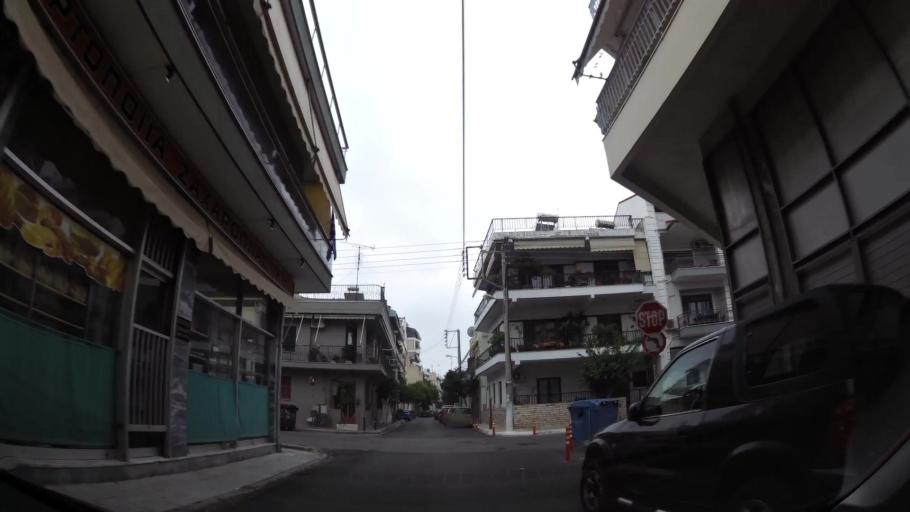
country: GR
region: Attica
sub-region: Nomarchia Athinas
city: Peristeri
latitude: 38.0037
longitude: 23.6945
